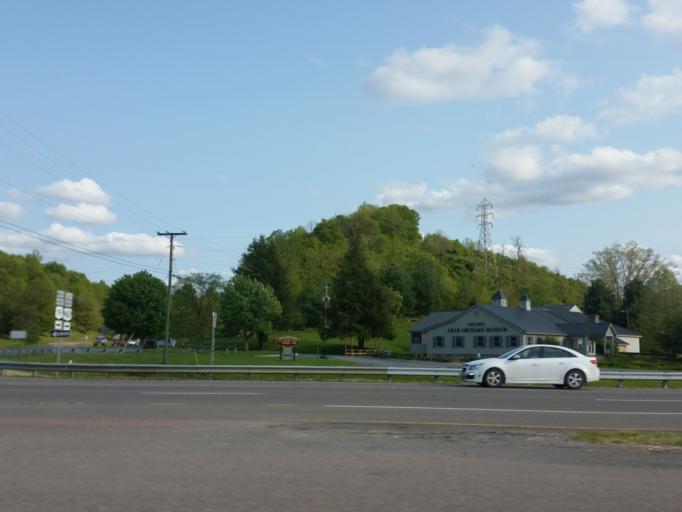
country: US
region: Virginia
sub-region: Tazewell County
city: Tazewell
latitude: 37.1206
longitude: -81.5743
